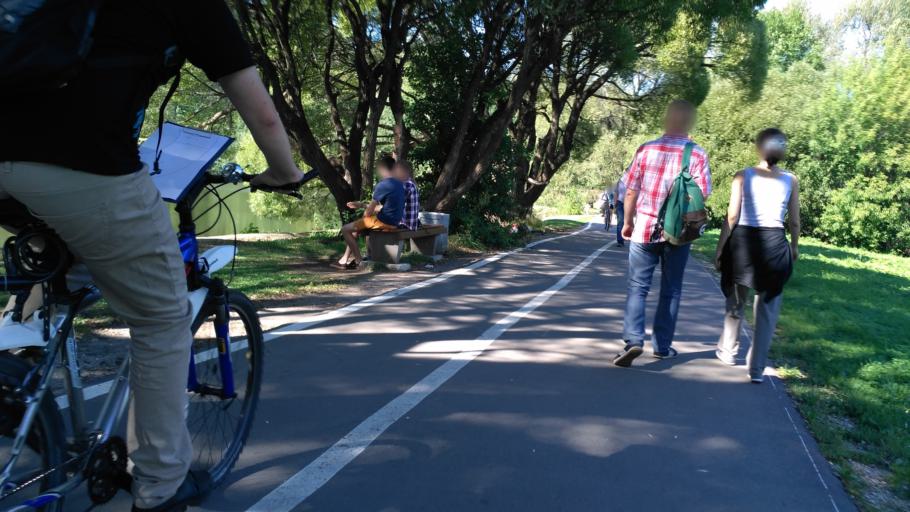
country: RU
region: Moskovskaya
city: Izmaylovo
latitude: 55.7794
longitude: 37.7764
